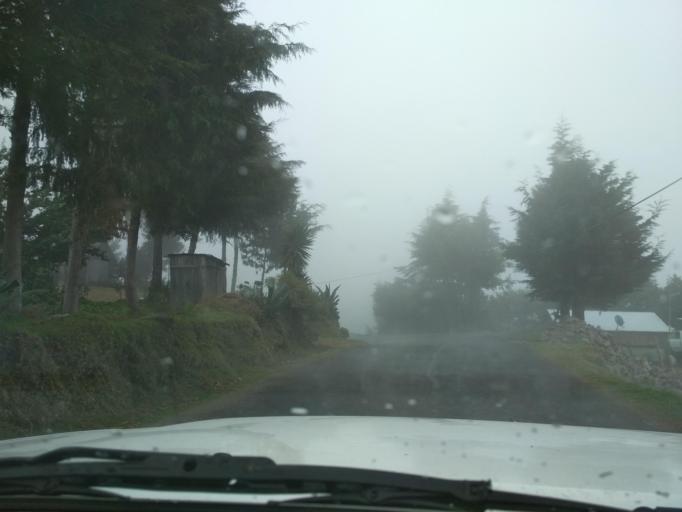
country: MX
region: Veracruz
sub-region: Mariano Escobedo
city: San Isidro el Berro
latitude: 18.9297
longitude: -97.2153
